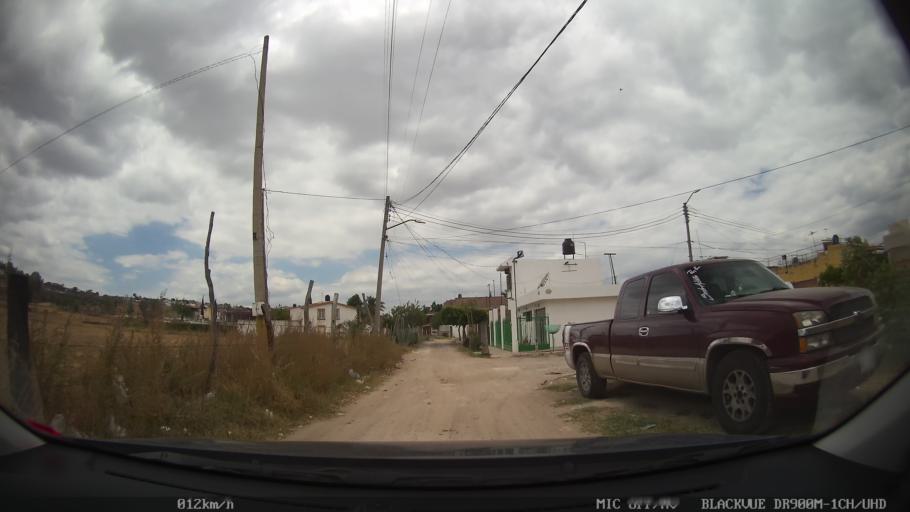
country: MX
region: Jalisco
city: Tonala
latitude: 20.6429
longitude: -103.2501
